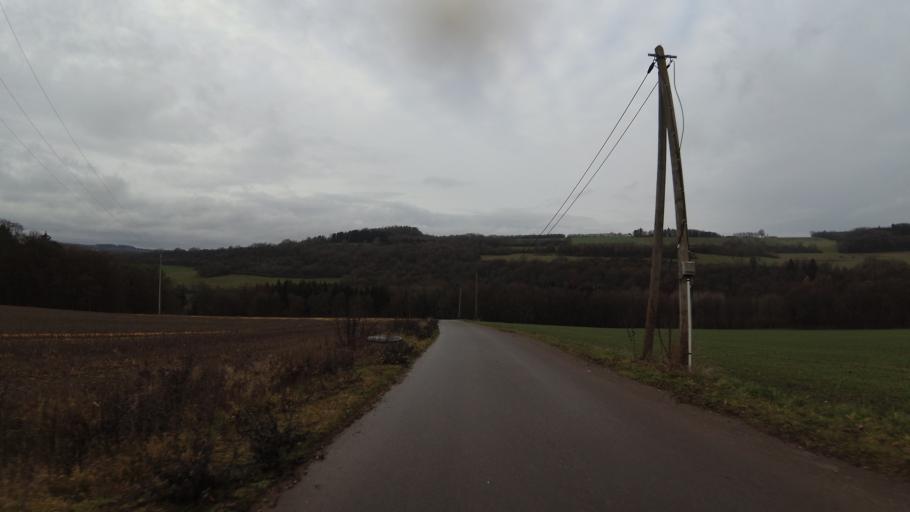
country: DE
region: Rheinland-Pfalz
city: Breitenbach
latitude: 49.4461
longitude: 7.2547
